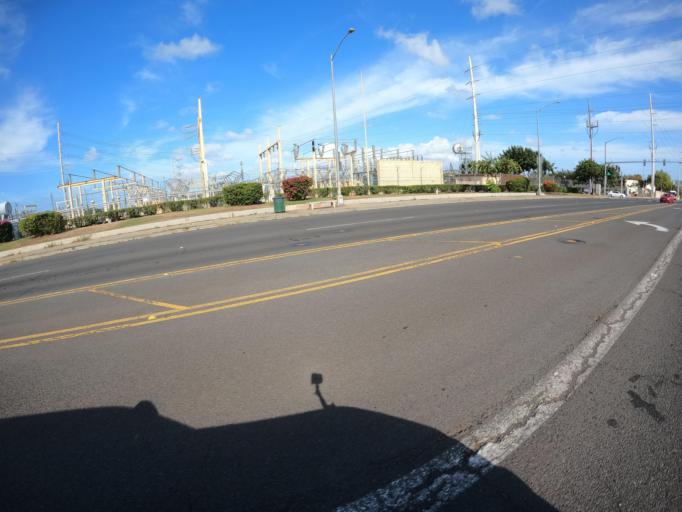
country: US
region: Hawaii
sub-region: Honolulu County
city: Halawa
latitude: 21.3576
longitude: -157.9267
